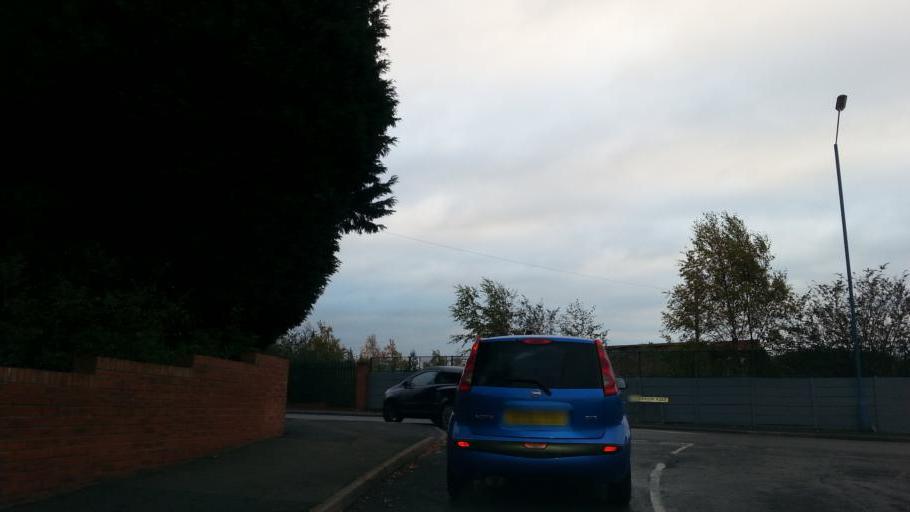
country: GB
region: England
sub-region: Sandwell
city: Wednesbury
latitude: 52.5466
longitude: -2.0348
